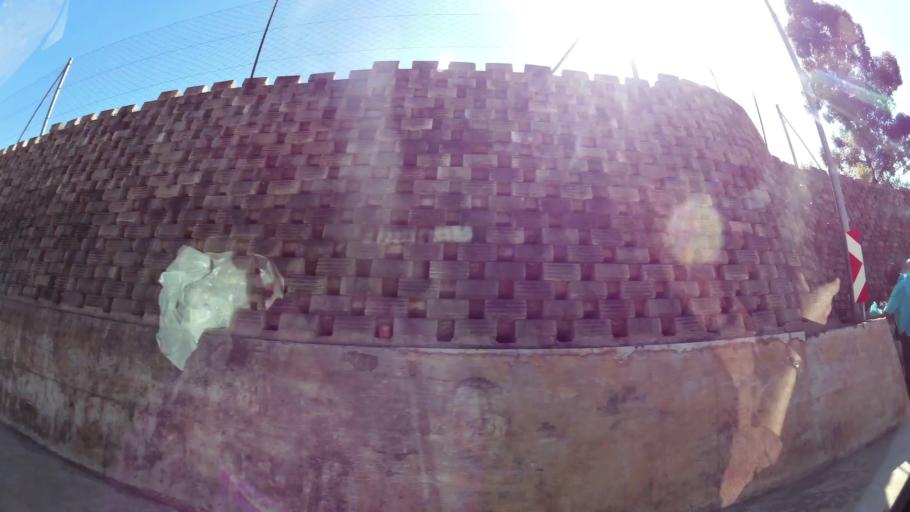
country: ZA
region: Limpopo
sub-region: Mopani District Municipality
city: Tzaneen
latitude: -23.8222
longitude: 30.1558
